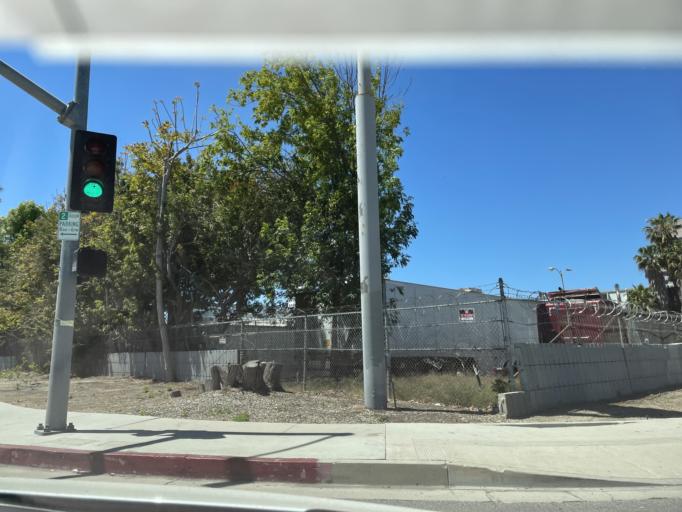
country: US
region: California
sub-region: Los Angeles County
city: Canoga Park
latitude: 34.1883
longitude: -118.5929
